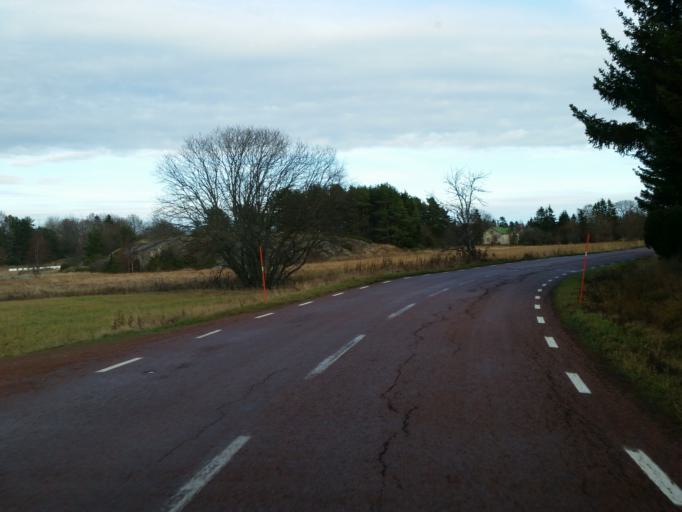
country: AX
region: Alands skaergard
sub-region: Kumlinge
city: Kumlinge
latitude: 60.2574
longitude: 20.7696
